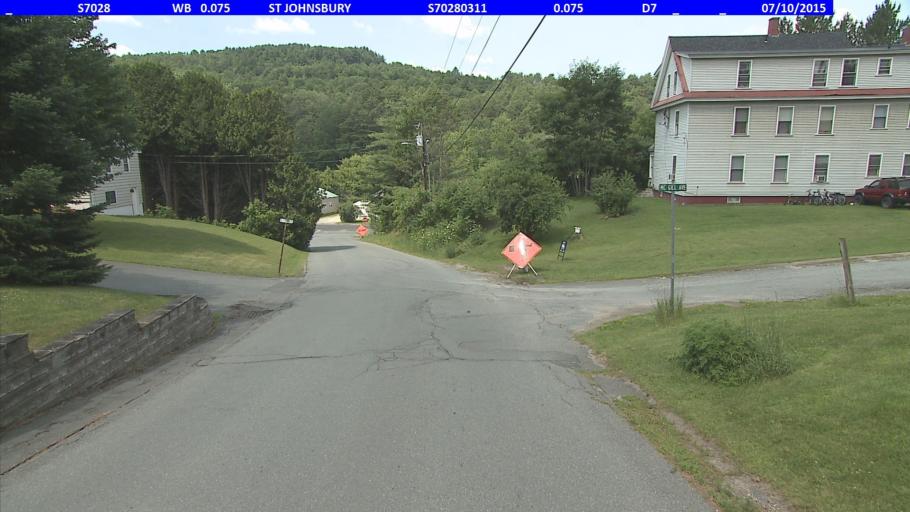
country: US
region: Vermont
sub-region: Caledonia County
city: St Johnsbury
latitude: 44.4330
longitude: -72.0158
